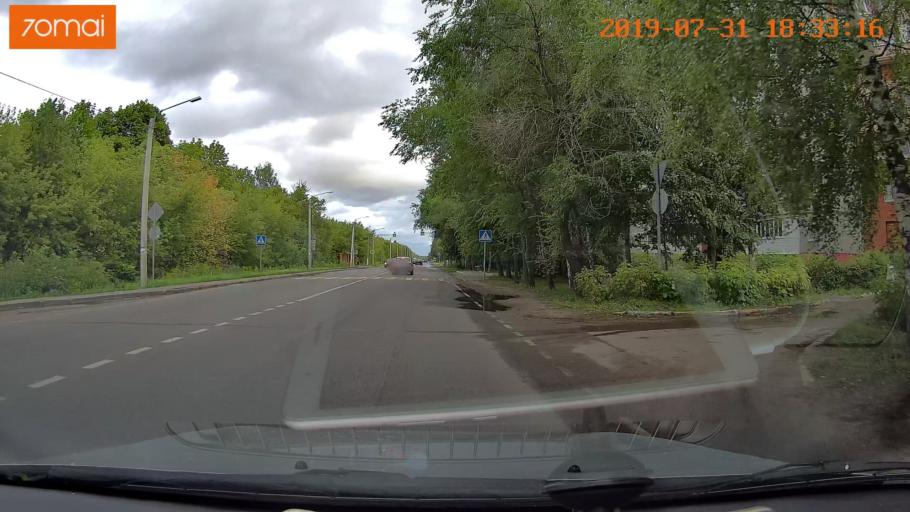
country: RU
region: Moskovskaya
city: Voskresensk
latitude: 55.3113
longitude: 38.6551
